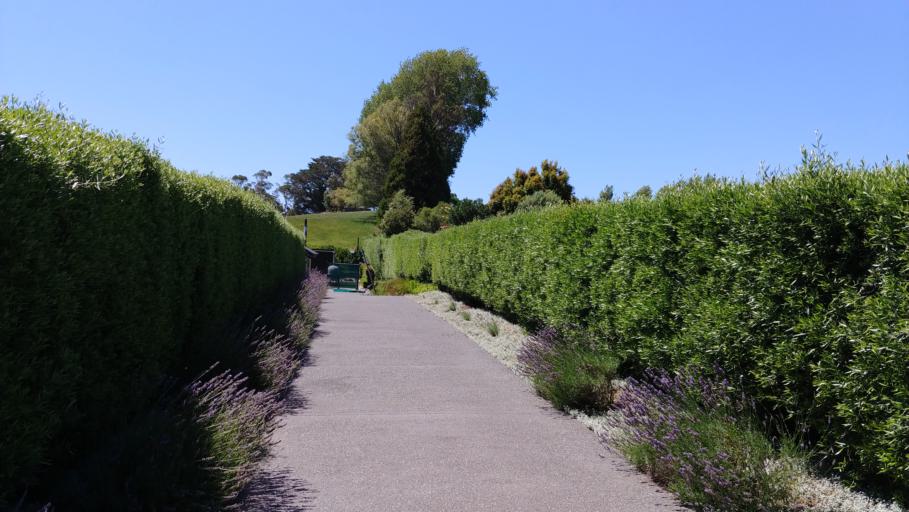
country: NZ
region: Bay of Plenty
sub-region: Tauranga City
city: Tauranga
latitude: -37.7855
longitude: 176.1383
